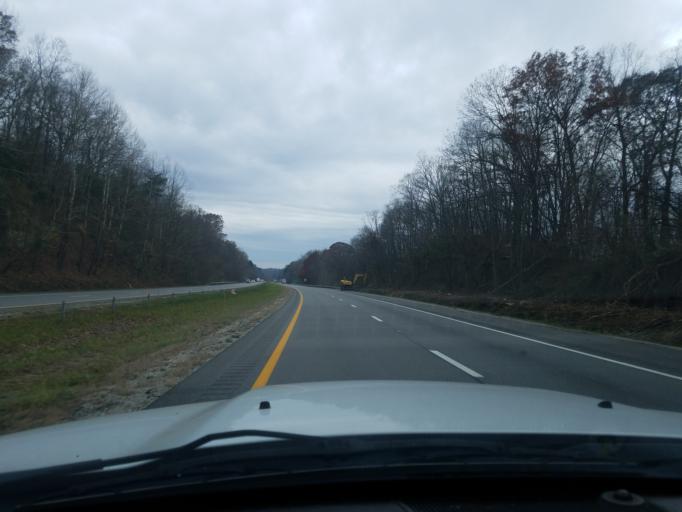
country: US
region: Ohio
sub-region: Lawrence County
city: Burlington
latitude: 38.3943
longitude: -82.5367
